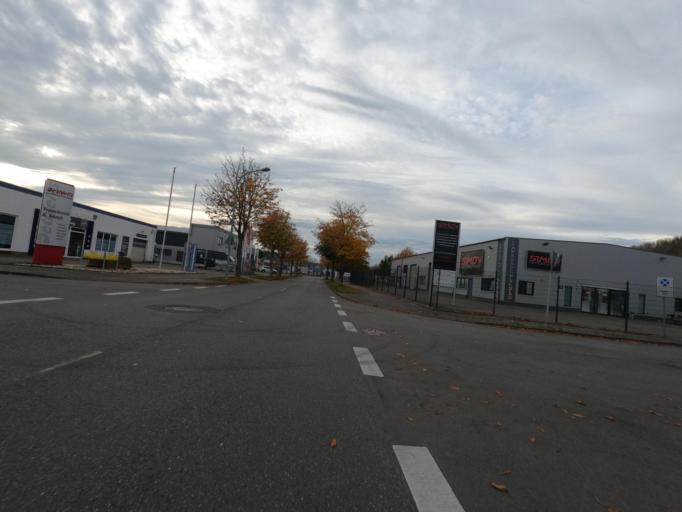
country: DE
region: North Rhine-Westphalia
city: Huckelhoven
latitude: 51.0522
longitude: 6.2120
